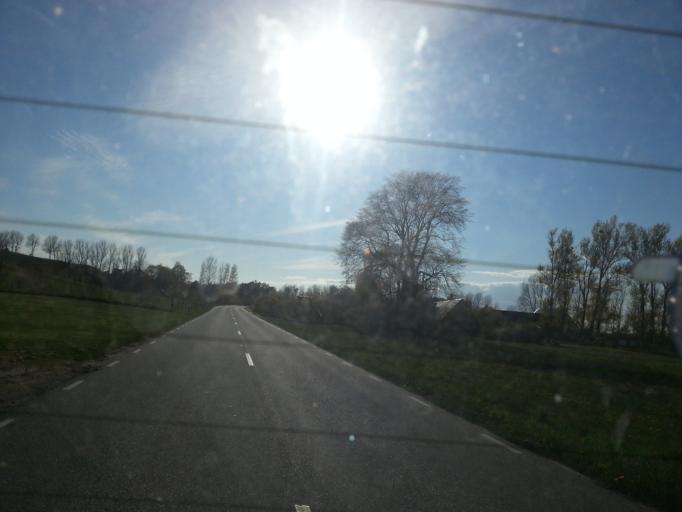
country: SE
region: Skane
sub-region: Ystads Kommun
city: Kopingebro
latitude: 55.3910
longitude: 14.1046
